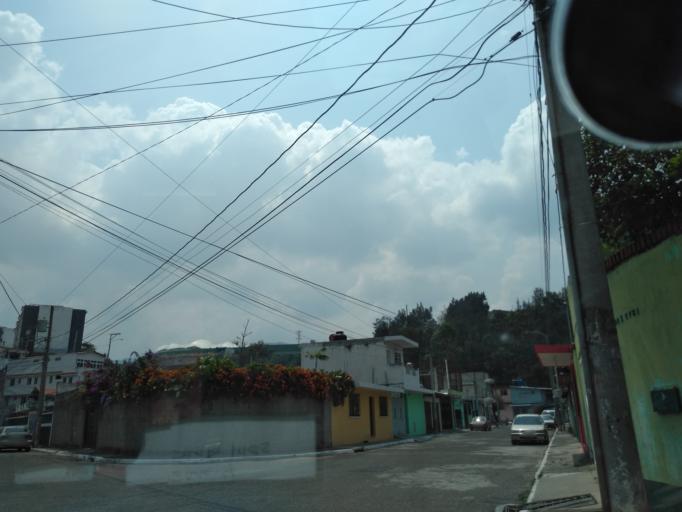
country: GT
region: Guatemala
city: Petapa
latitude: 14.5236
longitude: -90.5386
